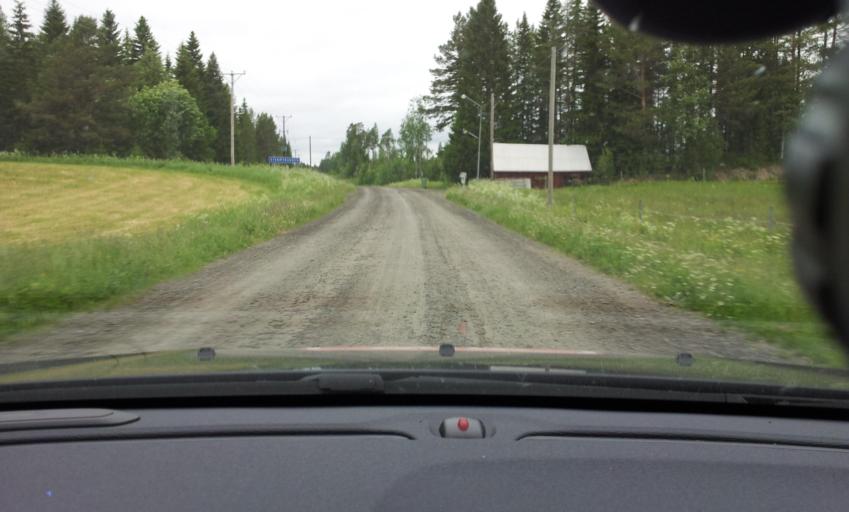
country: SE
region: Jaemtland
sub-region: Krokoms Kommun
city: Valla
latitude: 63.2556
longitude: 13.9450
